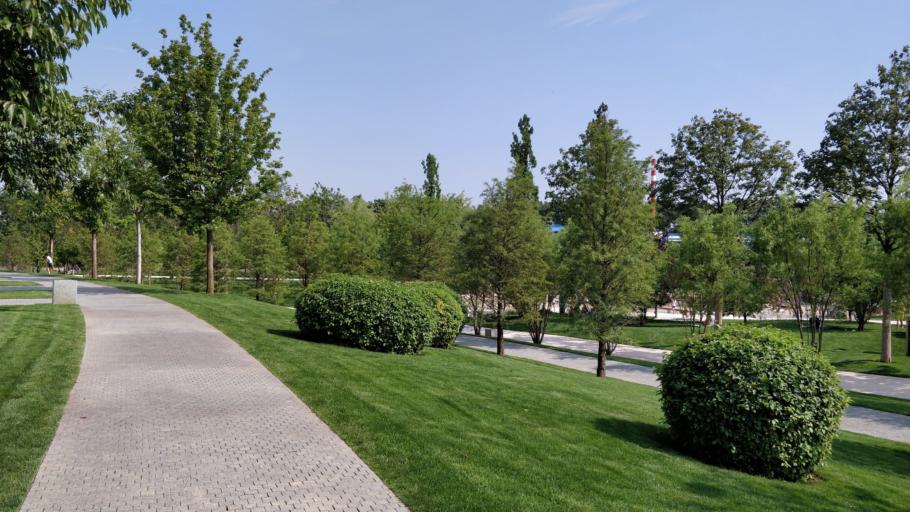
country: RU
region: Krasnodarskiy
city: Krasnodar
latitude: 45.0400
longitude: 39.0309
